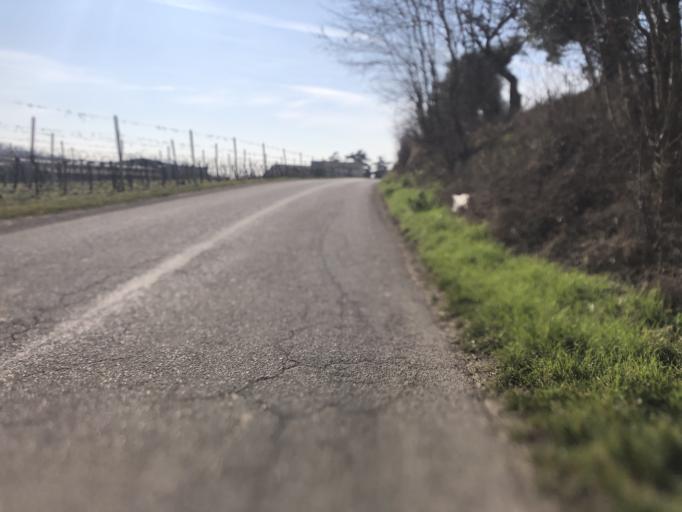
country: IT
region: Veneto
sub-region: Provincia di Verona
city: San Giorgio in Salici
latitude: 45.4033
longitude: 10.7775
